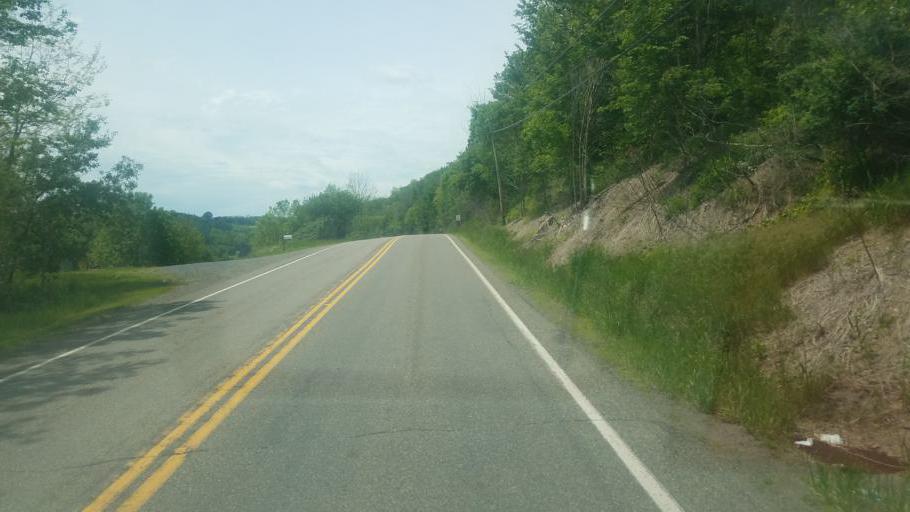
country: US
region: Pennsylvania
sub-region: Tioga County
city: Wellsboro
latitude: 41.7416
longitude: -77.3269
